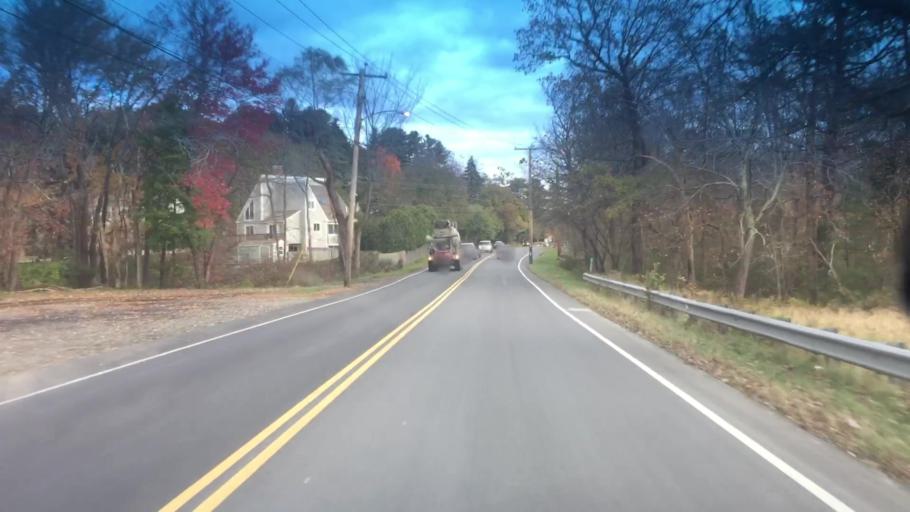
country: US
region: Massachusetts
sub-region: Norfolk County
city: Medfield
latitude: 42.1831
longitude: -71.3190
